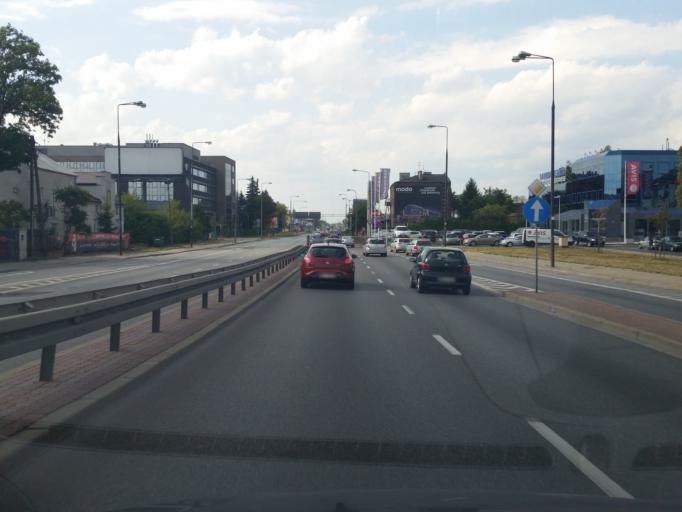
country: PL
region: Masovian Voivodeship
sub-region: Warszawa
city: Wlochy
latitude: 52.1908
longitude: 20.9555
